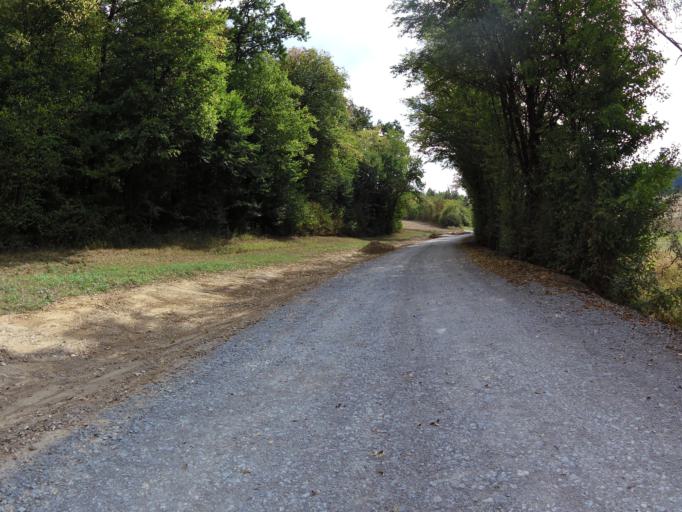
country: DE
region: Bavaria
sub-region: Regierungsbezirk Unterfranken
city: Hettstadt
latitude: 49.7855
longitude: 9.8042
